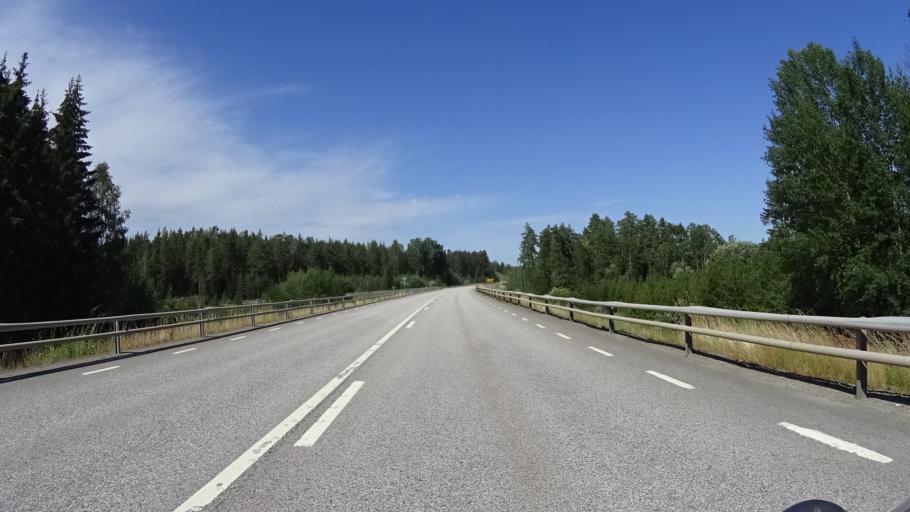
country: SE
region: Kalmar
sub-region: Vasterviks Kommun
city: Gamleby
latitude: 57.9265
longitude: 16.3754
